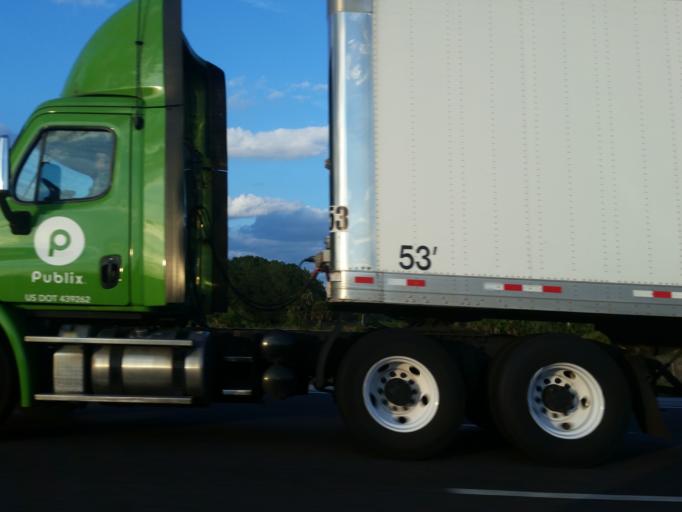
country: US
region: Florida
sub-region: Sarasota County
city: Osprey
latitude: 27.2063
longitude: -82.4418
